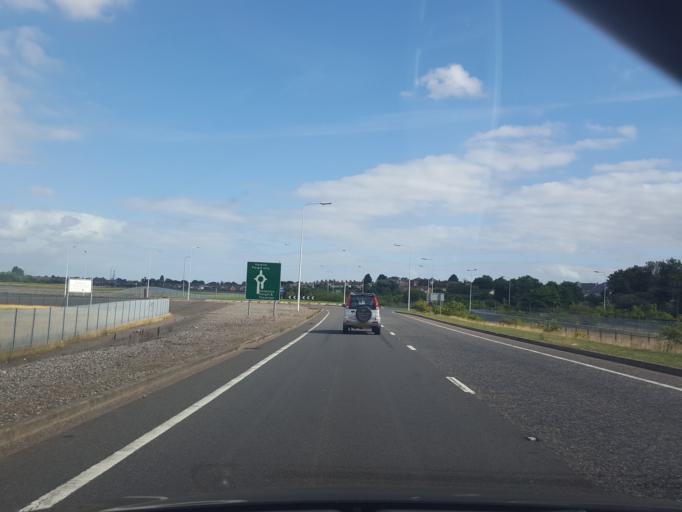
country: GB
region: England
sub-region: Essex
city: Dovercourt
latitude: 51.9397
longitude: 1.2691
